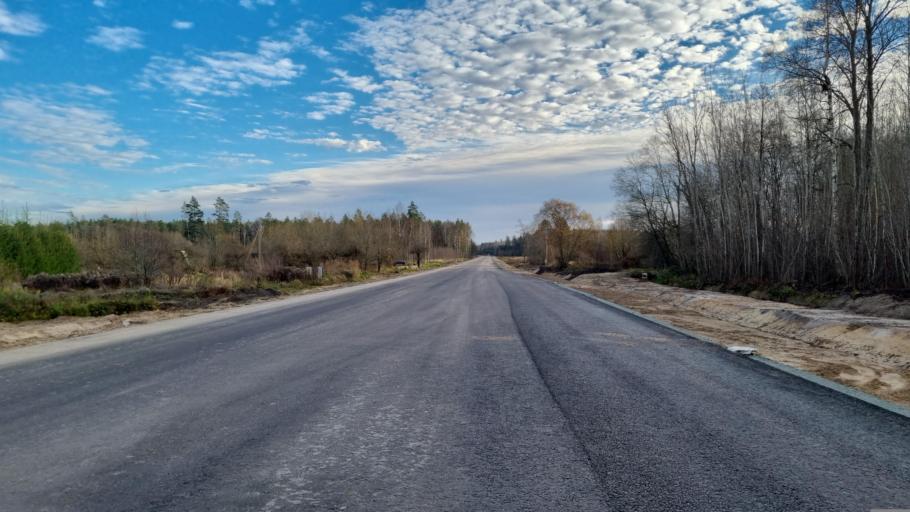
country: LV
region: Kekava
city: Kekava
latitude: 56.8028
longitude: 24.2020
